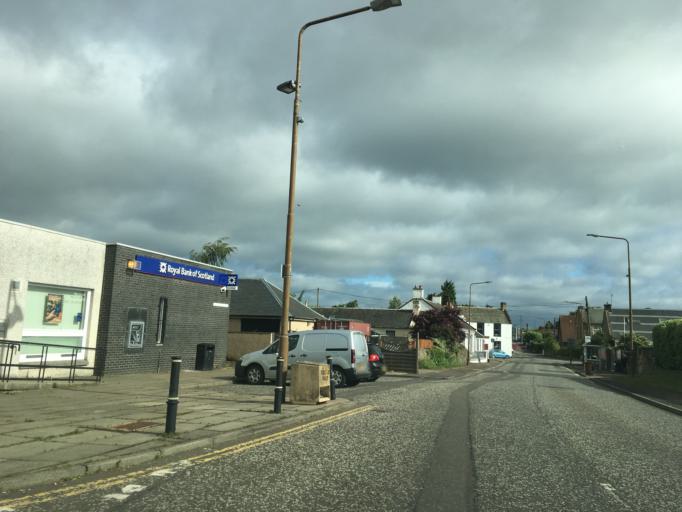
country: GB
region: Scotland
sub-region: Edinburgh
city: Newbridge
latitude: 55.9383
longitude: -3.4079
